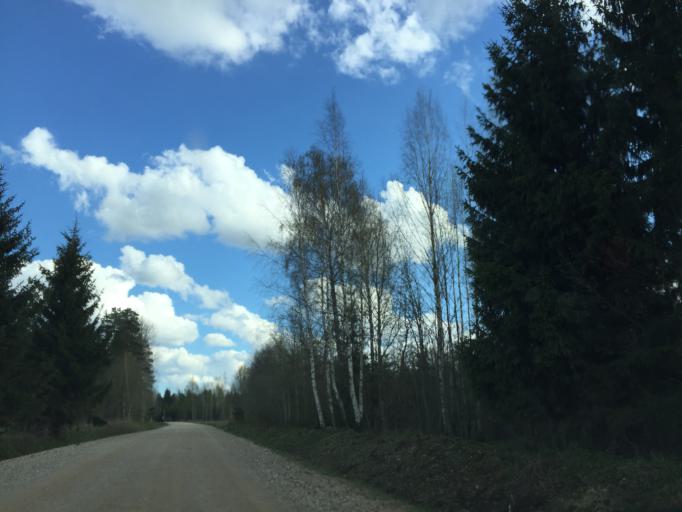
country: LV
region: Beverina
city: Murmuiza
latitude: 57.4651
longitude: 25.5010
